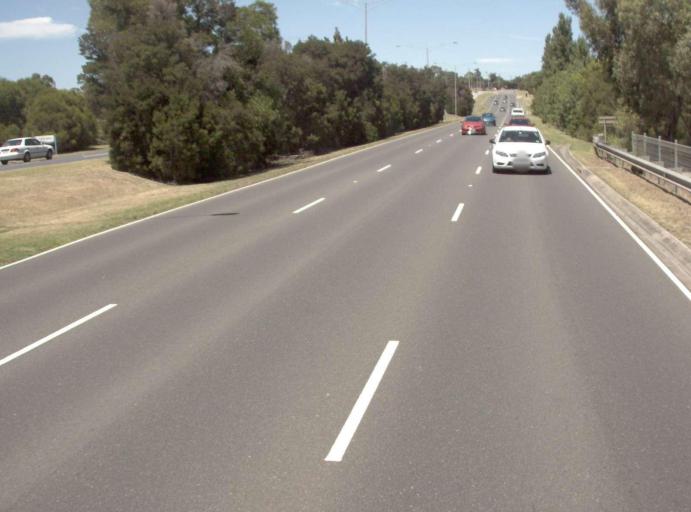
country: AU
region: Victoria
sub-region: Casey
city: Hallam
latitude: -38.0118
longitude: 145.2847
